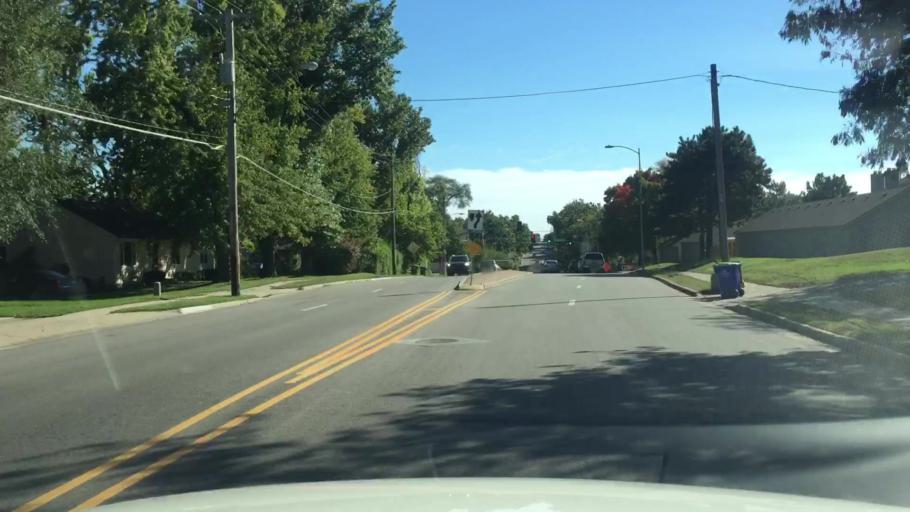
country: US
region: Kansas
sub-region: Johnson County
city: Shawnee
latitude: 39.0240
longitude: -94.7240
